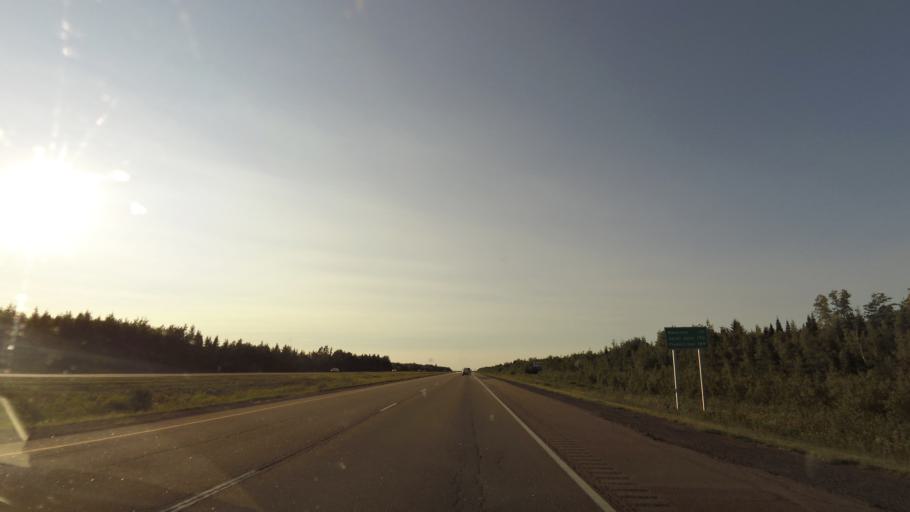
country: CA
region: New Brunswick
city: Dieppe
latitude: 46.1099
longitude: -64.6118
